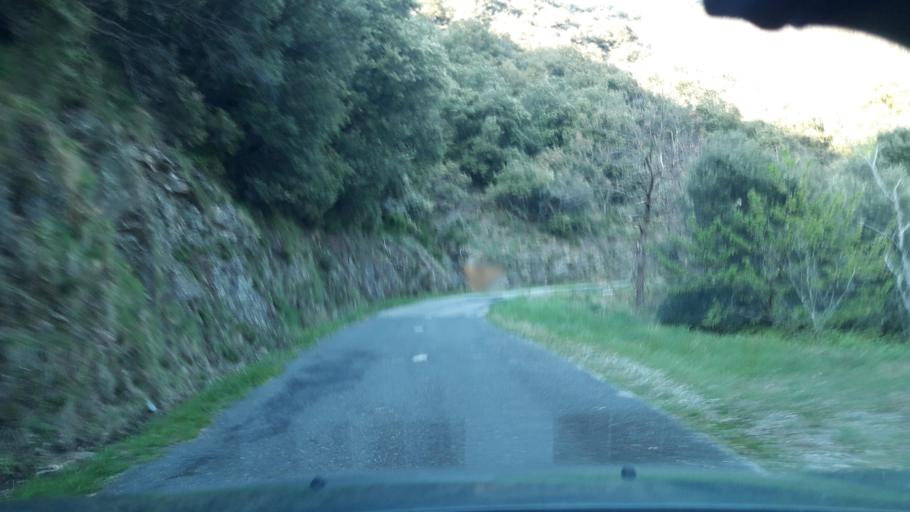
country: FR
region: Languedoc-Roussillon
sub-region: Departement du Gard
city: Valleraugue
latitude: 44.1014
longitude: 3.6415
